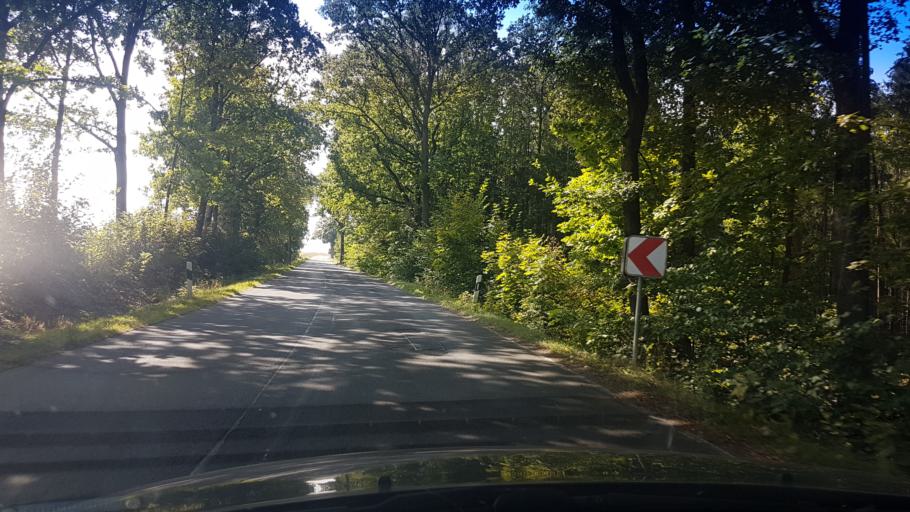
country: DE
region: Bavaria
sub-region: Upper Franconia
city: Hohenberg an der Eger
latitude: 50.0789
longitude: 12.2050
